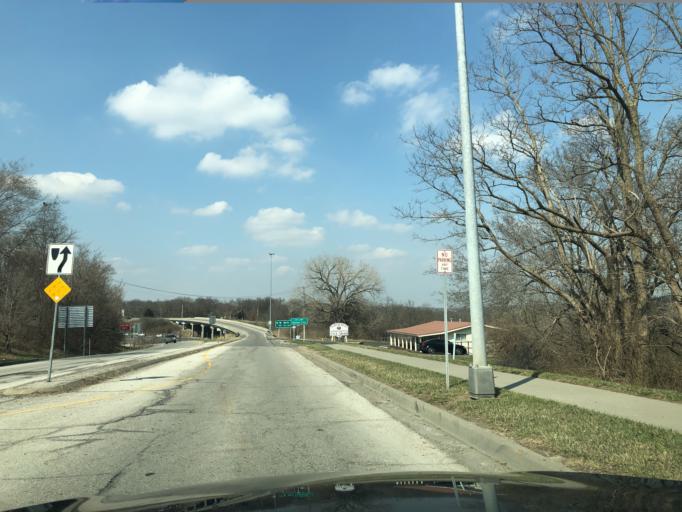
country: US
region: Missouri
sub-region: Platte County
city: Riverside
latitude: 39.1877
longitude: -94.6133
